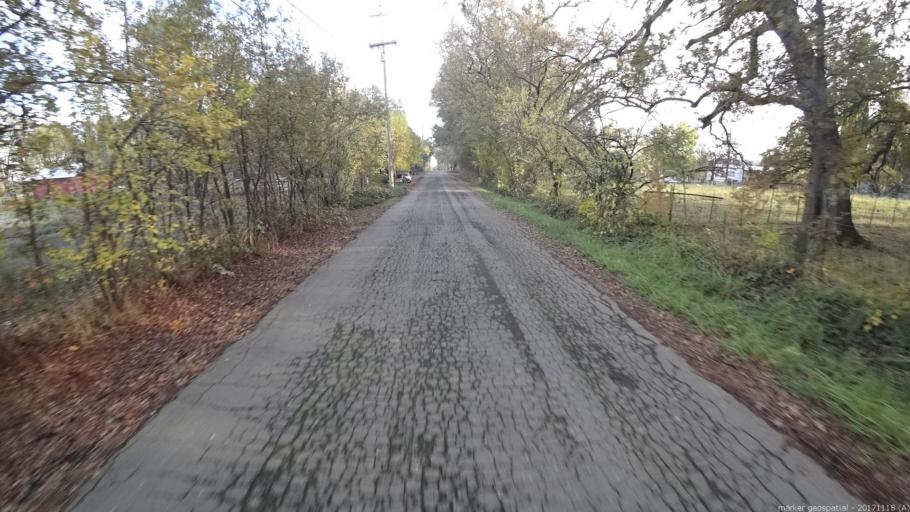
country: US
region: California
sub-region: Shasta County
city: Anderson
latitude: 40.4606
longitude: -122.3270
